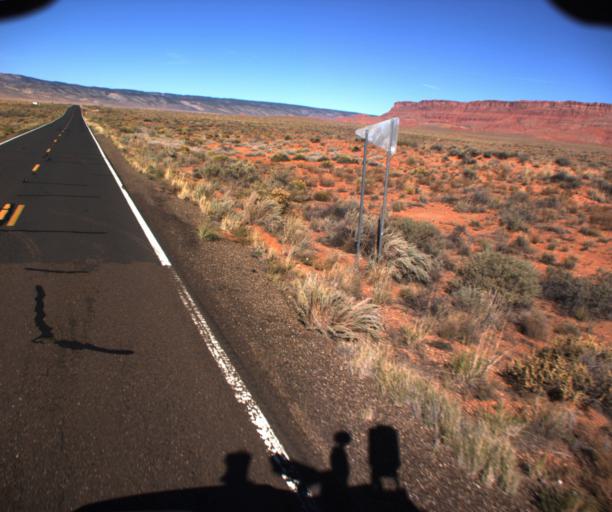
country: US
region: Arizona
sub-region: Coconino County
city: Page
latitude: 36.7041
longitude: -111.9435
